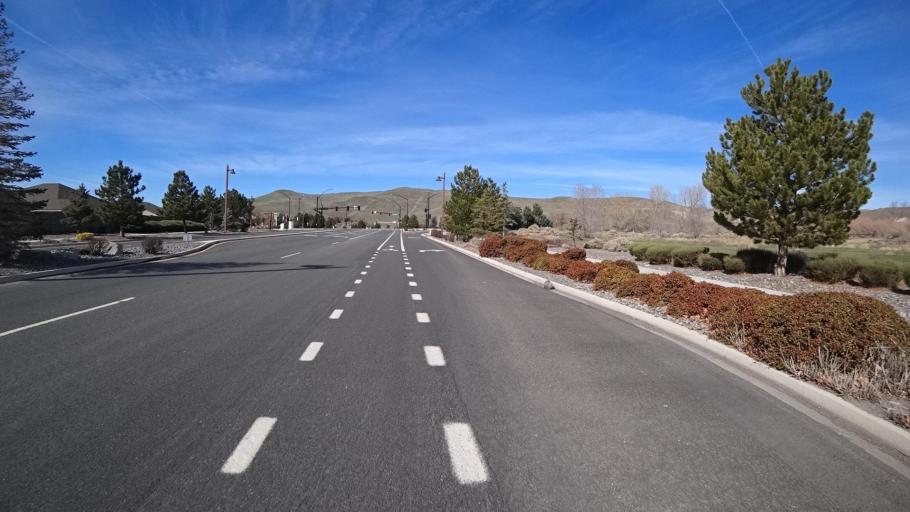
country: US
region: Nevada
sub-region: Washoe County
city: Sun Valley
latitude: 39.6045
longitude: -119.7281
